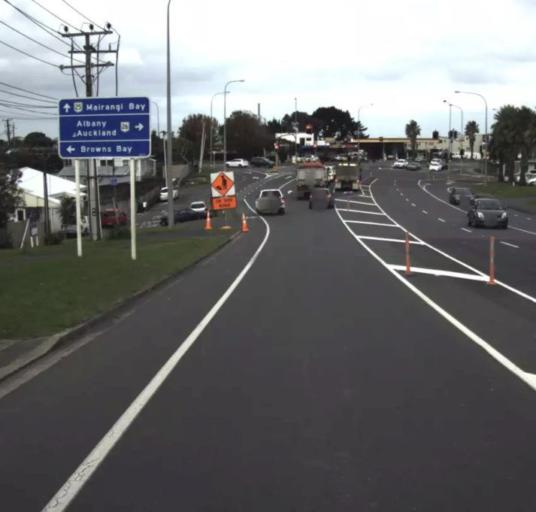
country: NZ
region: Auckland
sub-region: Auckland
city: Rothesay Bay
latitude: -36.7081
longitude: 174.7269
